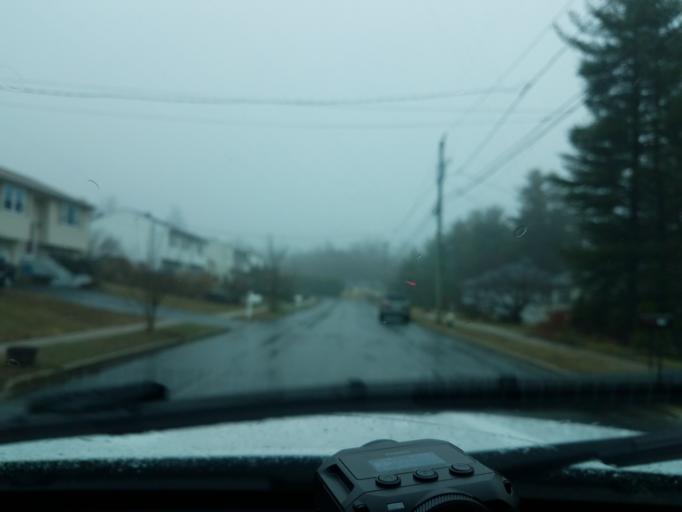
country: US
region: Connecticut
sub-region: New Haven County
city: Naugatuck
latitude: 41.4987
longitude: -73.0330
